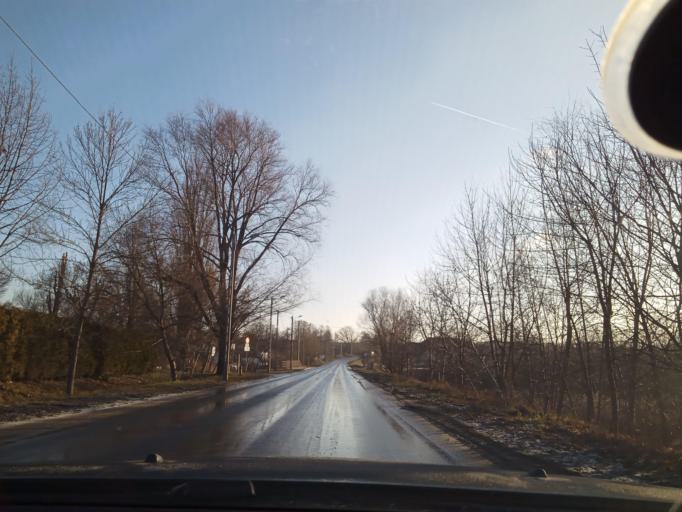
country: PL
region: Lesser Poland Voivodeship
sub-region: Powiat krakowski
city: Michalowice
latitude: 50.1061
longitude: 20.0442
